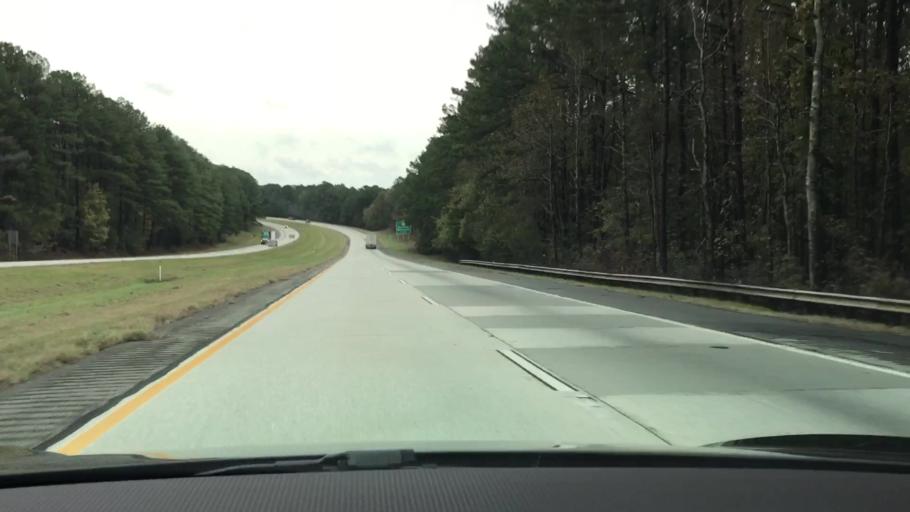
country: US
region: Georgia
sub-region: Taliaferro County
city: Crawfordville
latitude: 33.5000
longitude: -82.8201
